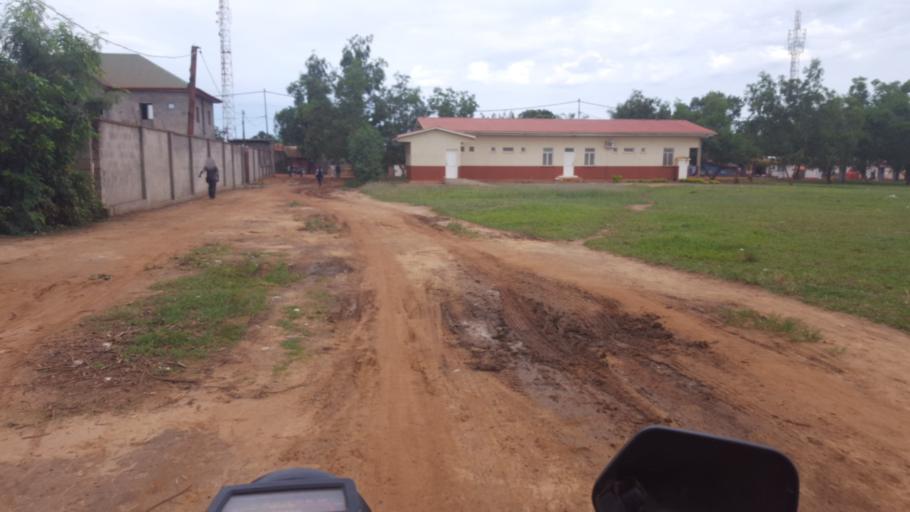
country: CD
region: Bandundu
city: Bandundu
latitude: -3.3015
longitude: 17.3766
